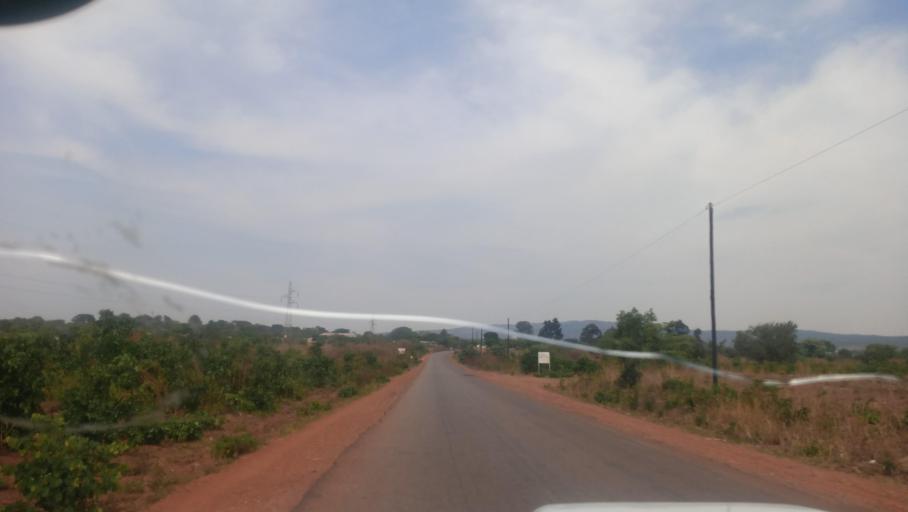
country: ZM
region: Northern
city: Mpika
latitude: -11.8330
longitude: 31.4172
